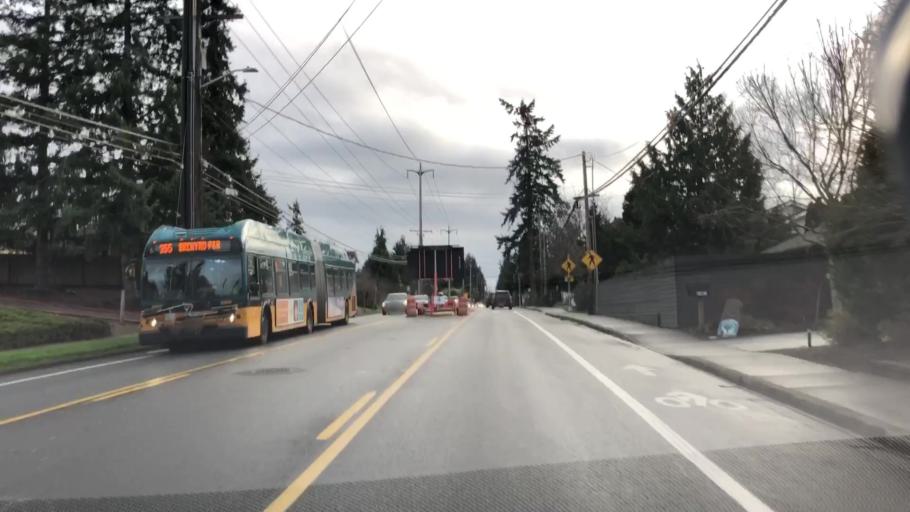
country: US
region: Washington
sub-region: King County
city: Kirkland
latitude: 47.6640
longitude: -122.1963
